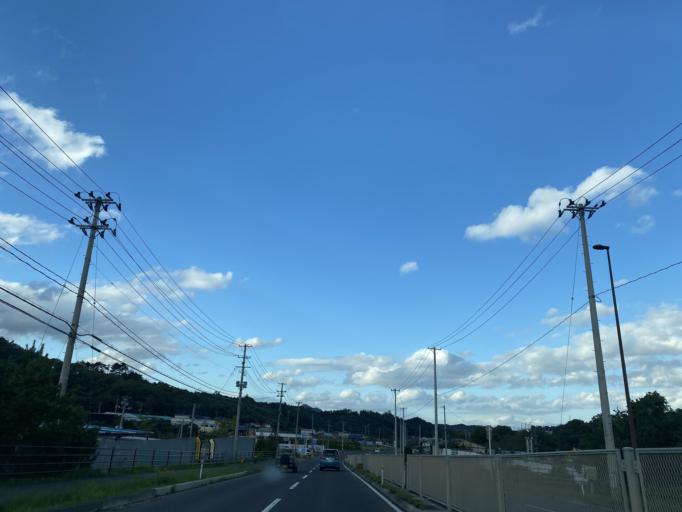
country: JP
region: Miyagi
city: Tomiya
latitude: 38.3737
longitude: 140.8556
